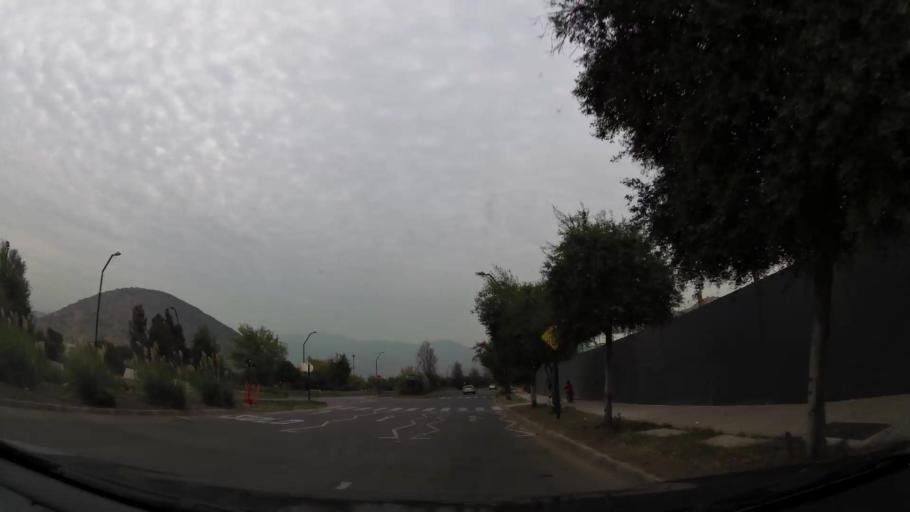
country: CL
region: Santiago Metropolitan
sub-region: Provincia de Chacabuco
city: Chicureo Abajo
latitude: -33.3066
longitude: -70.6634
